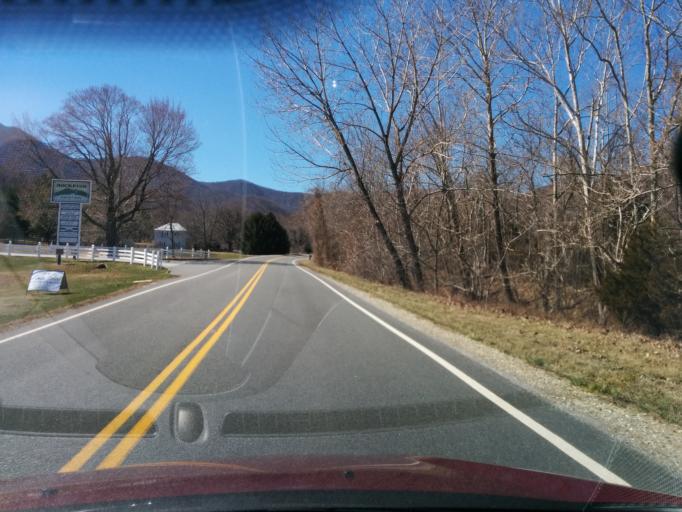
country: US
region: Virginia
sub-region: Nelson County
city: Nellysford
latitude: 37.8759
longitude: -78.9395
